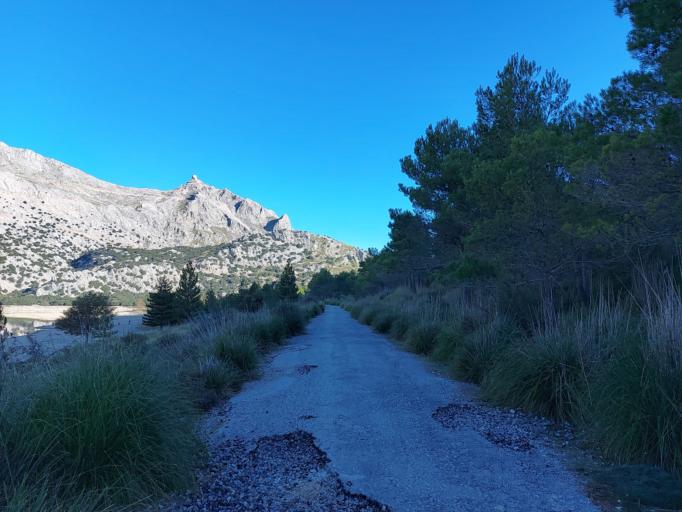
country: ES
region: Balearic Islands
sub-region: Illes Balears
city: Fornalutx
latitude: 39.7822
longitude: 2.7930
